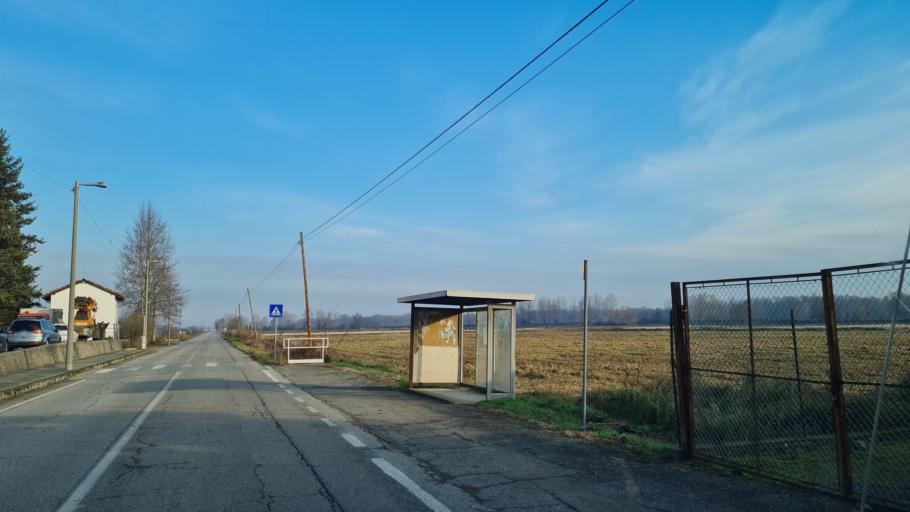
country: IT
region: Piedmont
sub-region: Provincia di Vercelli
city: Albano Vercellese
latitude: 45.4293
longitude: 8.3811
